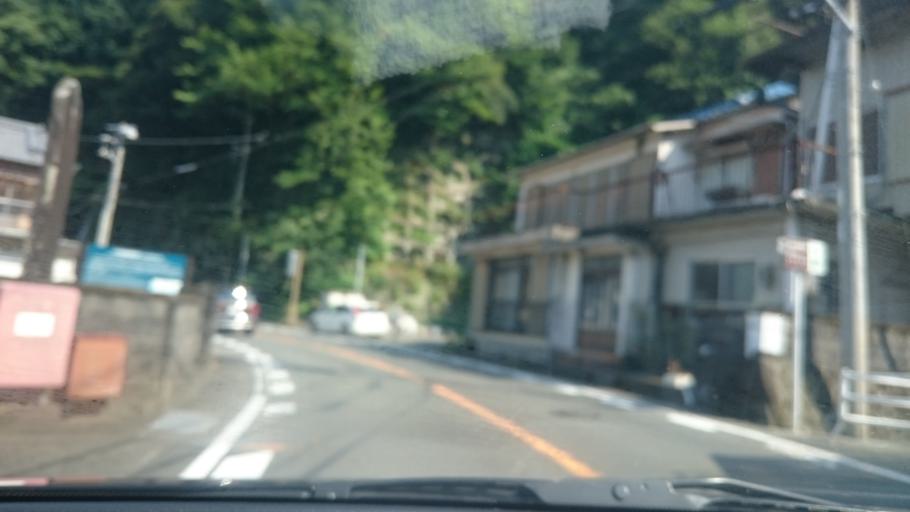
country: JP
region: Shizuoka
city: Heda
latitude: 34.9697
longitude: 138.7710
